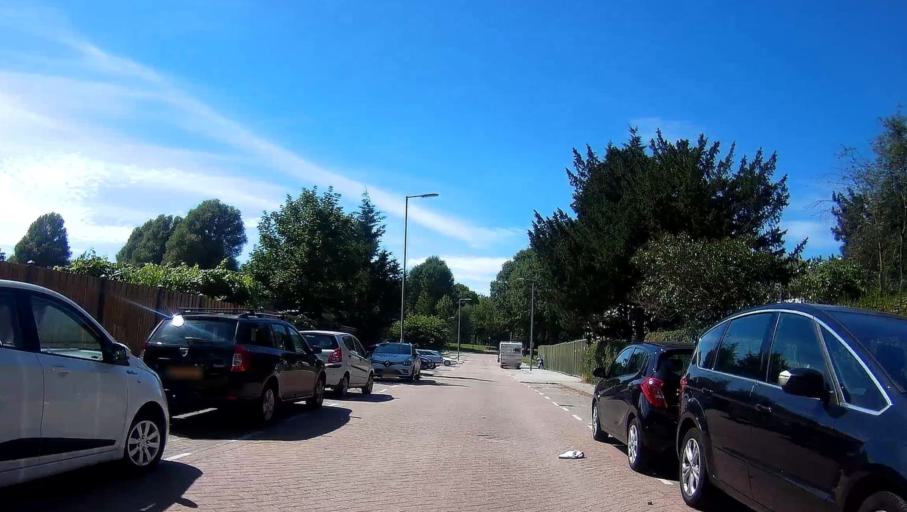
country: NL
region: South Holland
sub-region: Gemeente Capelle aan den IJssel
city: Capelle-West
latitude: 51.8932
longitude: 4.5492
